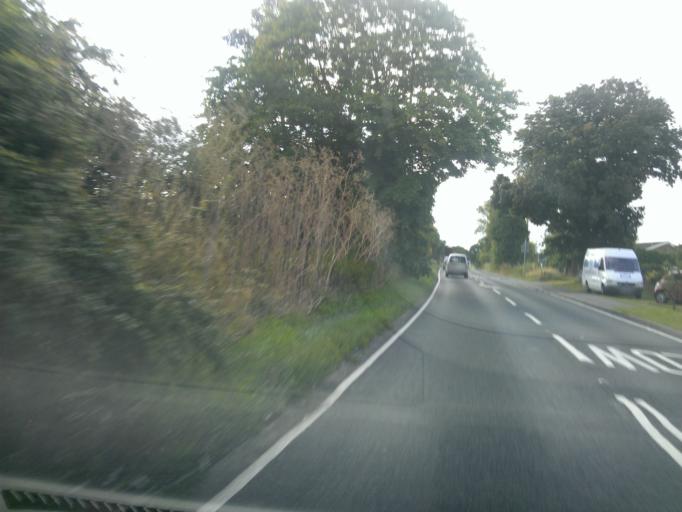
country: GB
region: England
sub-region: Essex
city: Saint Osyth
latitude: 51.8051
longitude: 1.0796
